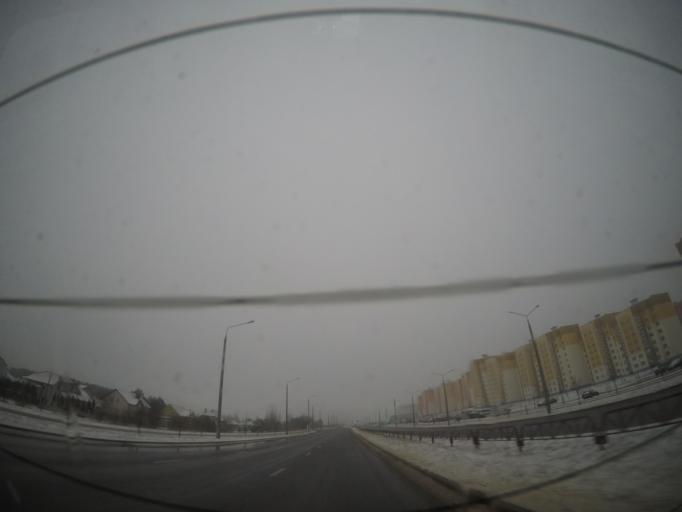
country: BY
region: Grodnenskaya
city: Hrodna
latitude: 53.6195
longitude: 23.8220
